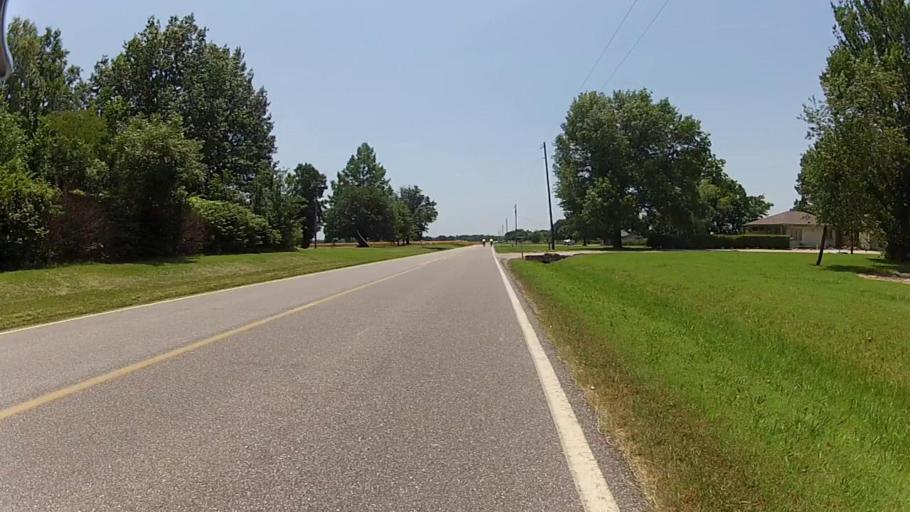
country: US
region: Kansas
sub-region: Montgomery County
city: Cherryvale
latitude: 37.2572
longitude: -95.5370
